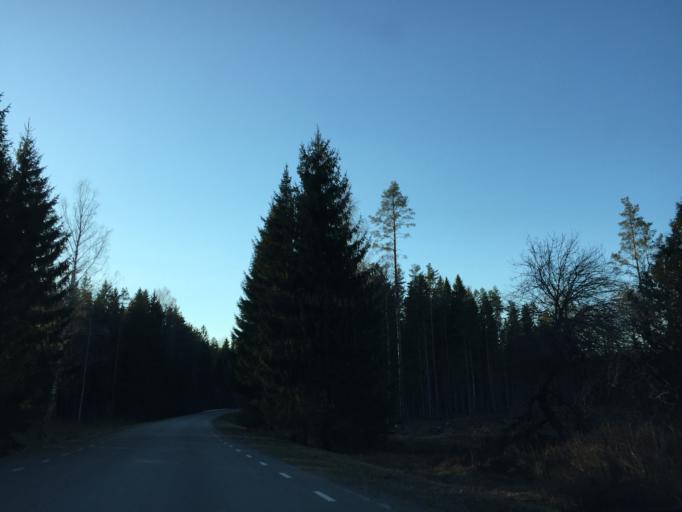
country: EE
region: Ida-Virumaa
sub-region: Toila vald
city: Voka
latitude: 59.1655
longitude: 27.5827
